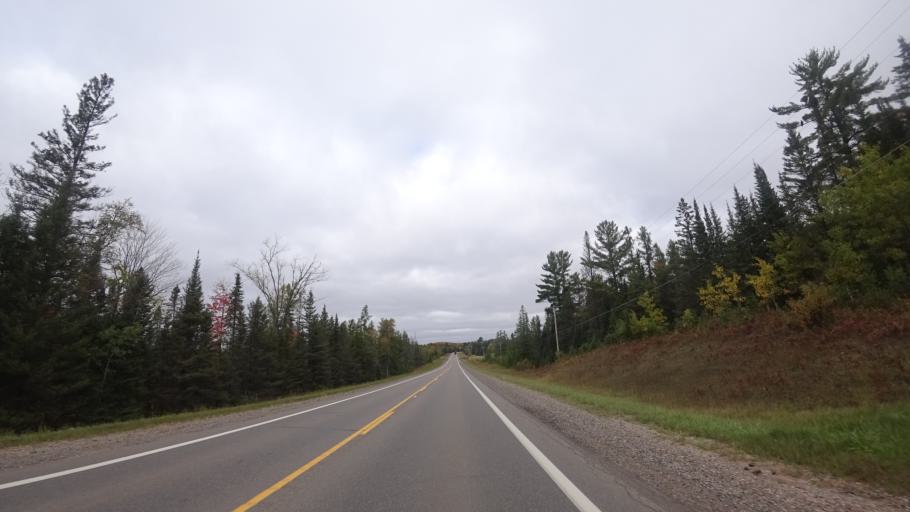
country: US
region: Michigan
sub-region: Iron County
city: Crystal Falls
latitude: 46.1175
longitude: -88.0871
